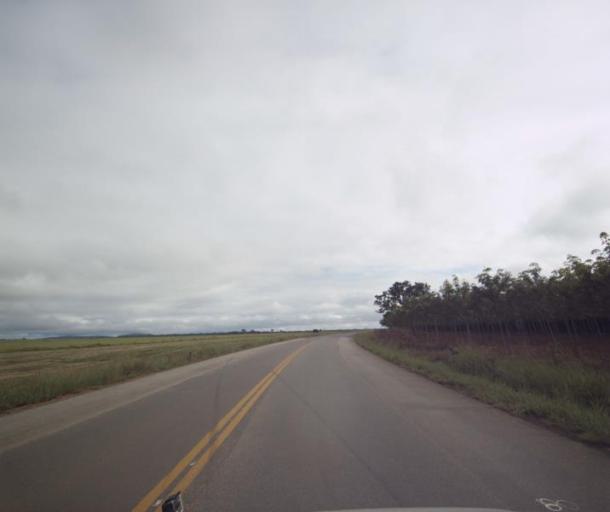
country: BR
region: Goias
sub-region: Padre Bernardo
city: Padre Bernardo
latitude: -15.3792
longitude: -48.6450
